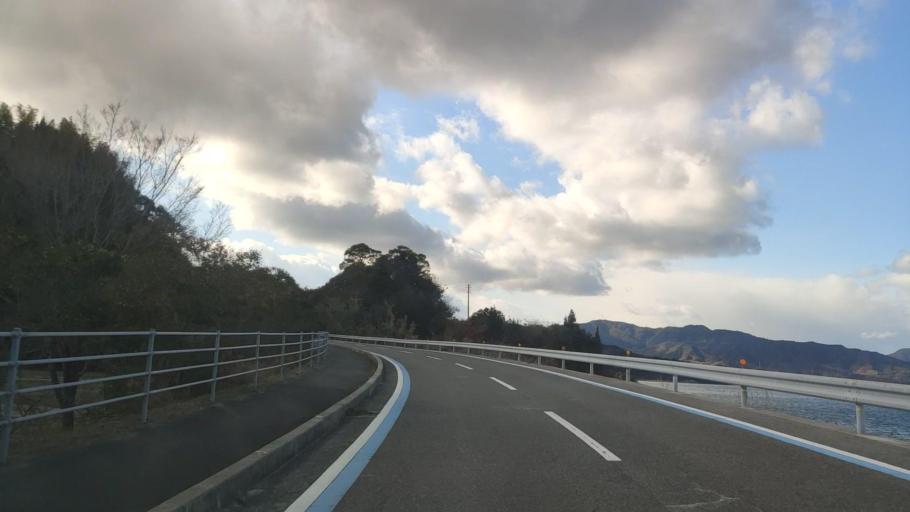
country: JP
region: Hiroshima
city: Innoshima
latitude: 34.2318
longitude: 133.0863
